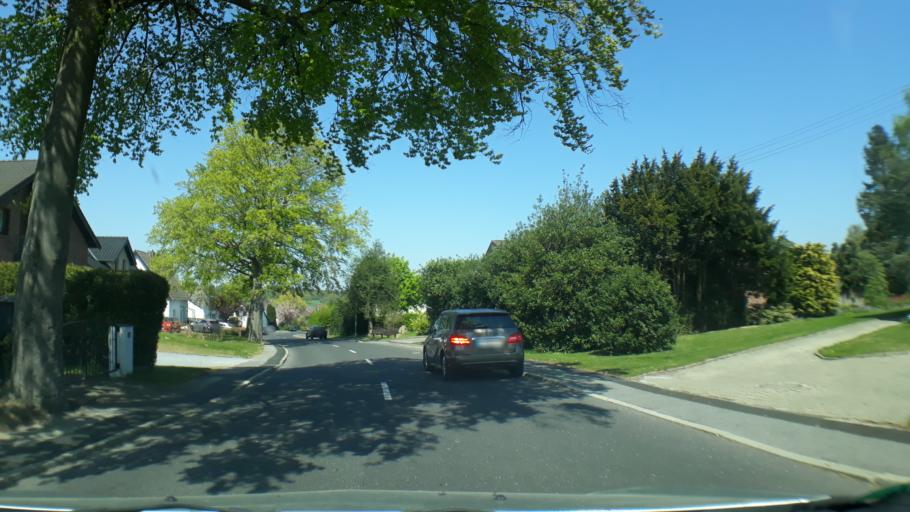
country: DE
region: North Rhine-Westphalia
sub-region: Regierungsbezirk Koln
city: Roetgen
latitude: 50.6475
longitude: 6.2002
